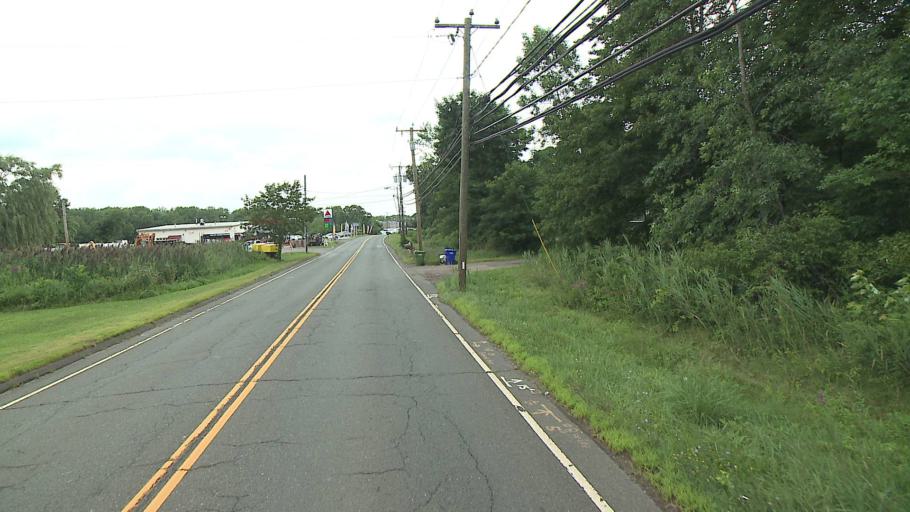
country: US
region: Connecticut
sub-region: Middlesex County
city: Cromwell
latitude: 41.5869
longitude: -72.6747
